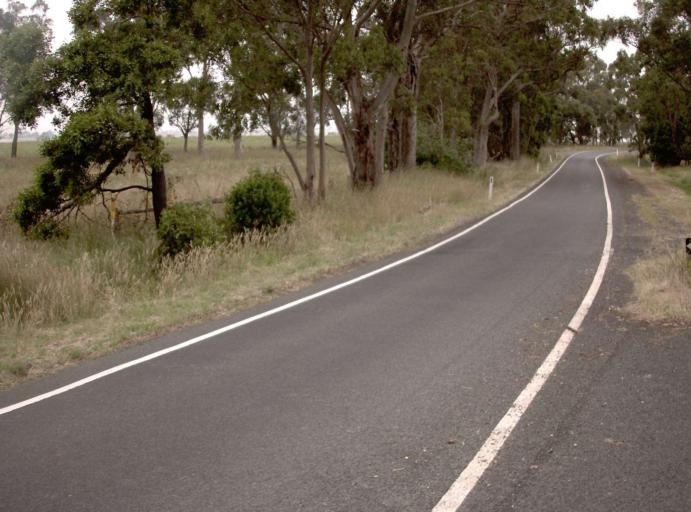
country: AU
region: Victoria
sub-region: Latrobe
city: Morwell
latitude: -38.2814
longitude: 146.3207
